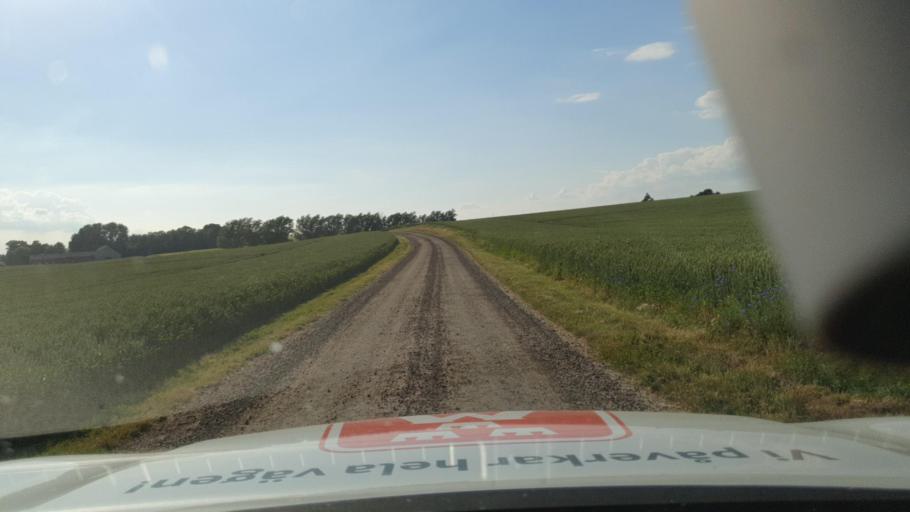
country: SE
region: Skane
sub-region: Skurups Kommun
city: Rydsgard
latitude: 55.4892
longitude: 13.5865
